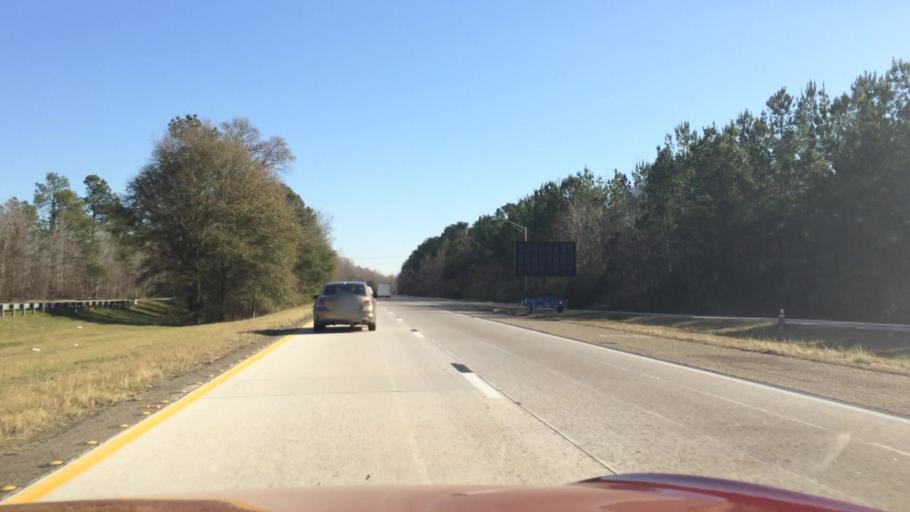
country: US
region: South Carolina
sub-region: Orangeburg County
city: Holly Hill
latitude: 33.2681
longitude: -80.4854
